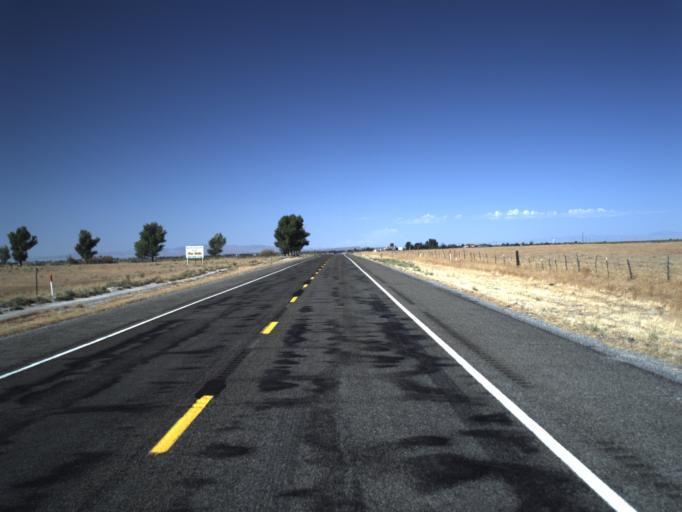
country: US
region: Utah
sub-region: Millard County
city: Delta
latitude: 39.3840
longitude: -112.5211
